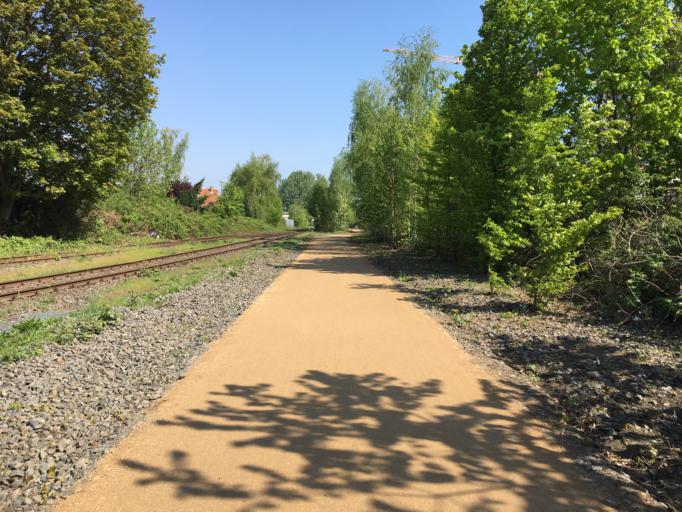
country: DE
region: Lower Saxony
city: Braunschweig
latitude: 52.2794
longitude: 10.5344
